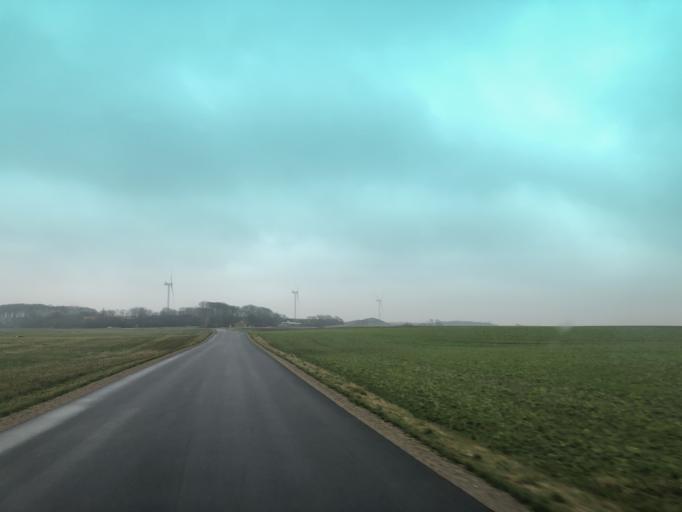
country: DK
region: Central Jutland
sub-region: Struer Kommune
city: Struer
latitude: 56.4321
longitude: 8.5914
